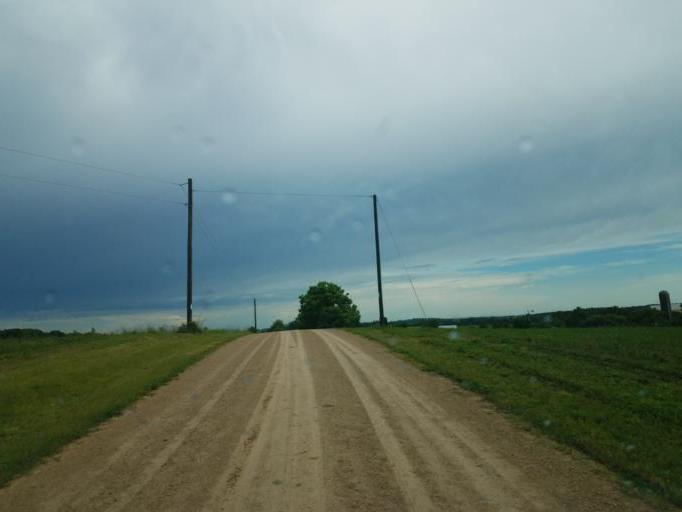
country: US
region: Wisconsin
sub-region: Vernon County
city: Hillsboro
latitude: 43.5883
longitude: -90.3820
